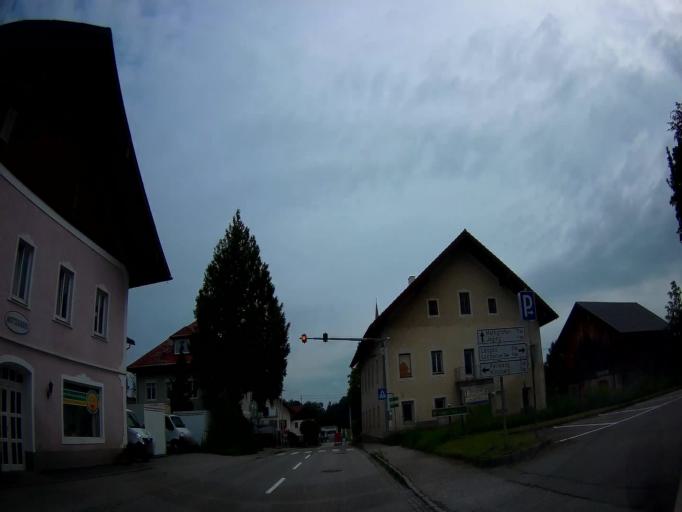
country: AT
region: Salzburg
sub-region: Politischer Bezirk Salzburg-Umgebung
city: Mattsee
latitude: 48.0148
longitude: 13.1270
